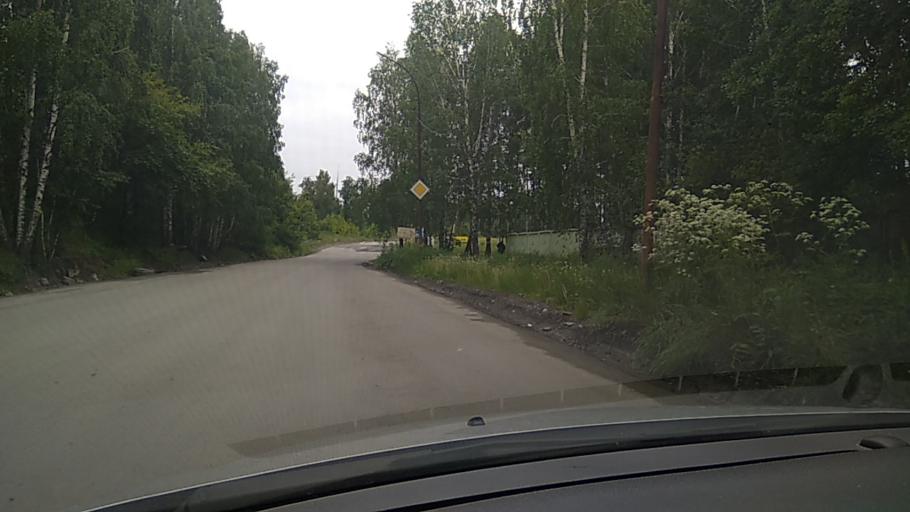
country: RU
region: Sverdlovsk
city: Shuvakish
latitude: 56.8921
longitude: 60.5166
